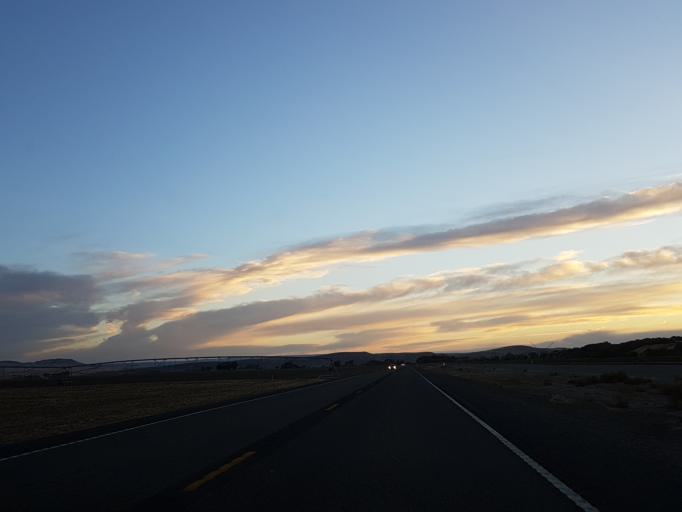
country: US
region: Oregon
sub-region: Malheur County
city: Vale
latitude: 43.9522
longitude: -117.2917
